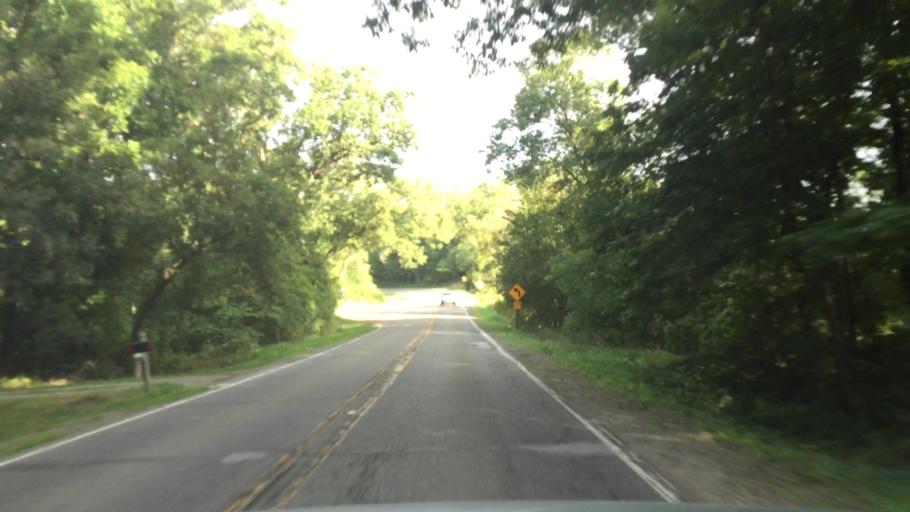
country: US
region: Michigan
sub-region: Livingston County
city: Brighton
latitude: 42.4880
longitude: -83.8524
